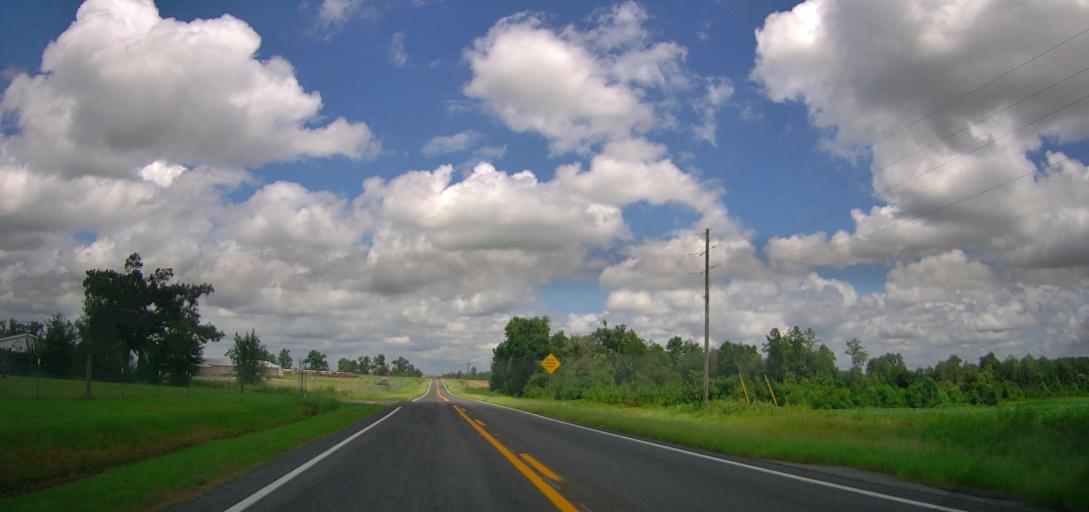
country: US
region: Georgia
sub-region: Turner County
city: Ashburn
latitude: 31.8047
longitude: -83.5758
